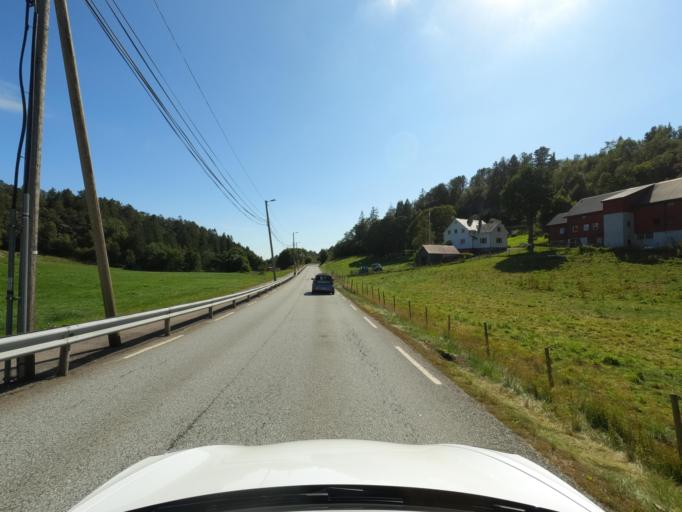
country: NO
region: Hordaland
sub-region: Bergen
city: Sandsli
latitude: 60.2361
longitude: 5.2998
